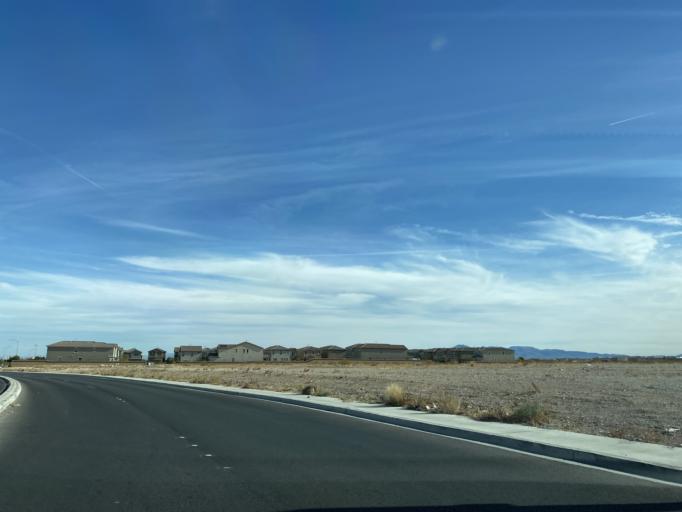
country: US
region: Nevada
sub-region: Clark County
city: Enterprise
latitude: 36.0477
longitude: -115.2789
